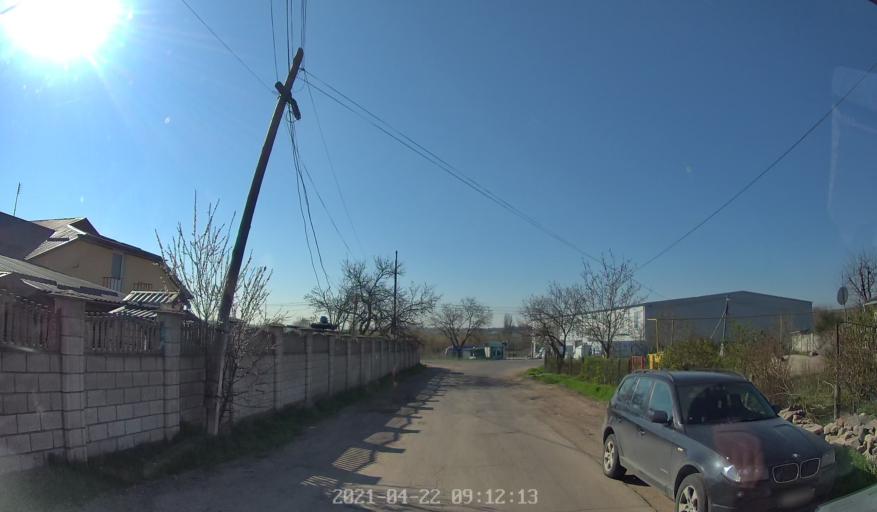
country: MD
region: Chisinau
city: Ciorescu
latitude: 47.1196
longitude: 28.8726
